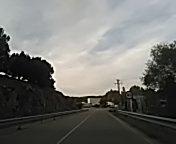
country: ES
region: Castille and Leon
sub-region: Provincia de Soria
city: San Leonardo de Yague
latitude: 41.8345
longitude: -3.0828
